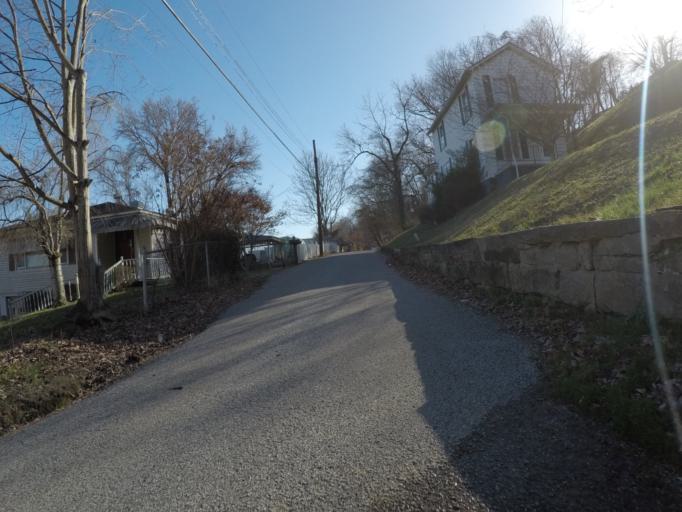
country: US
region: Kentucky
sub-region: Boyd County
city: Catlettsburg
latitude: 38.4173
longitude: -82.6010
